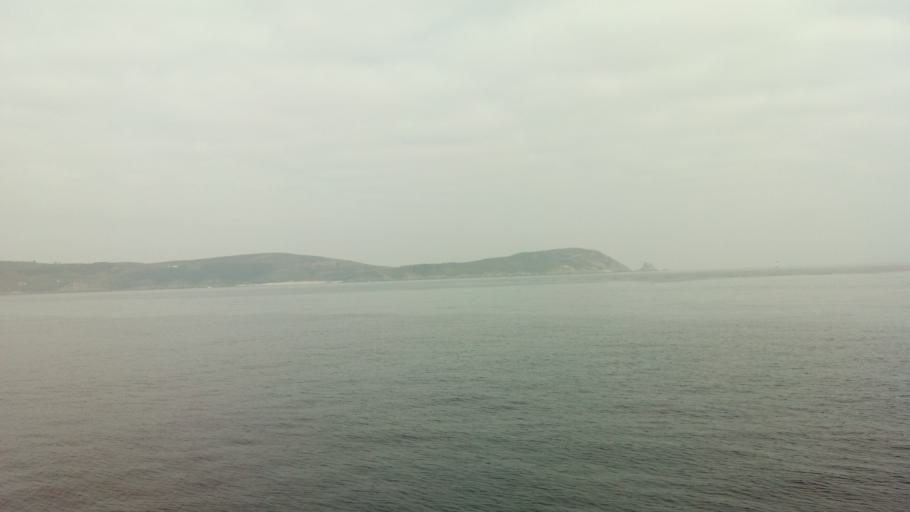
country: ES
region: Galicia
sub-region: Provincia de Pontevedra
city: Sanxenxo
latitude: 42.3793
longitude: -8.9032
